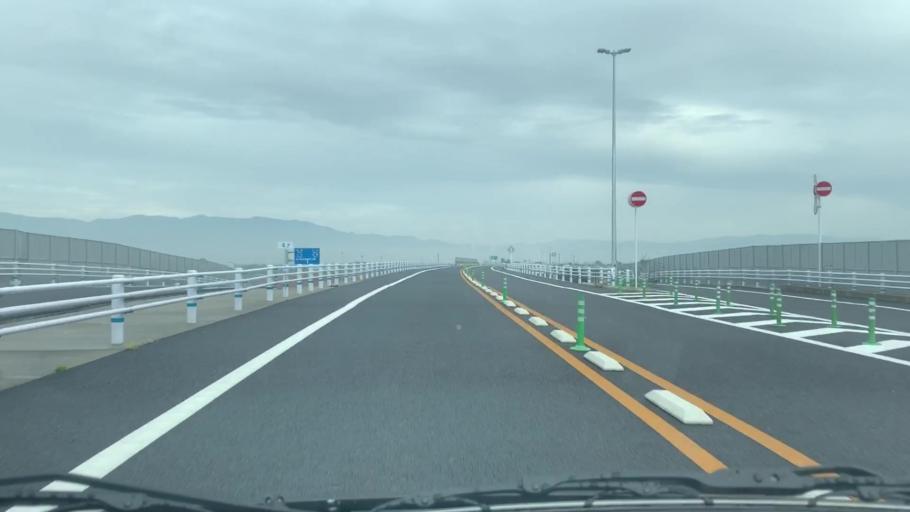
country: JP
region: Saga Prefecture
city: Saga-shi
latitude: 33.2190
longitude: 130.2144
